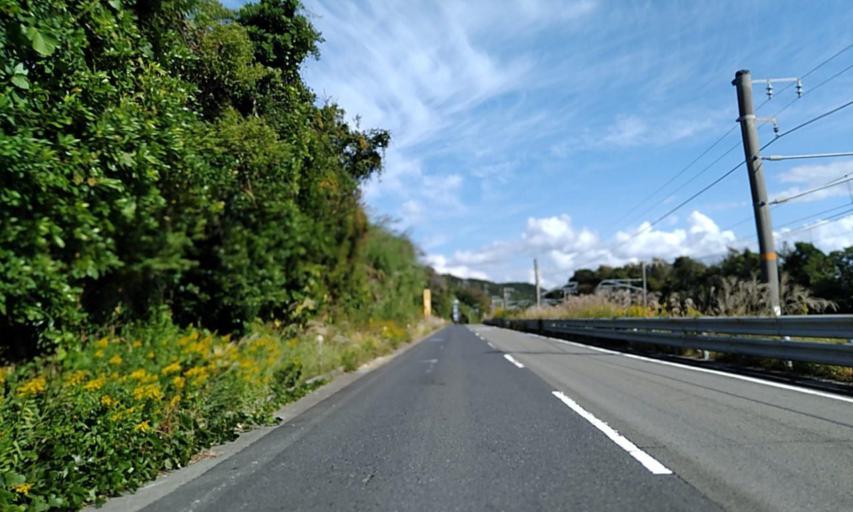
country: JP
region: Wakayama
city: Tanabe
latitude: 33.7831
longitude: 135.2525
